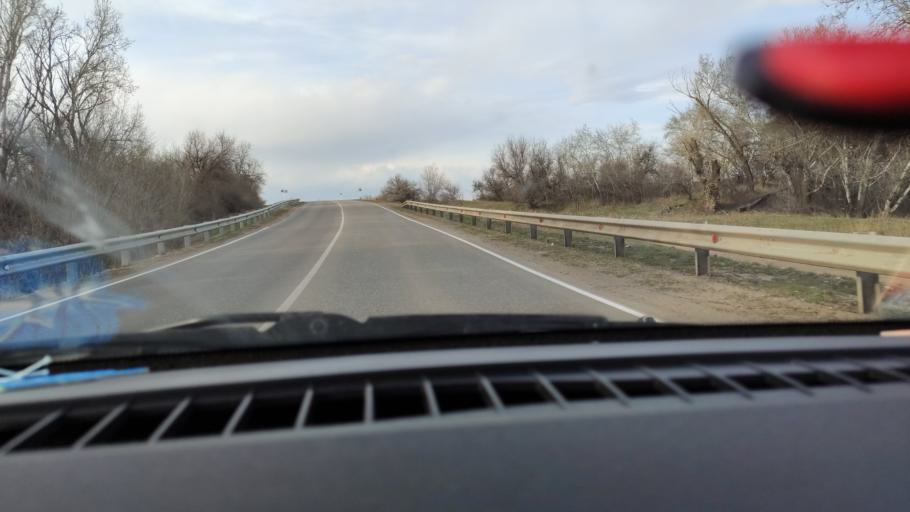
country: RU
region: Saratov
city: Privolzhskiy
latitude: 51.1959
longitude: 45.9154
